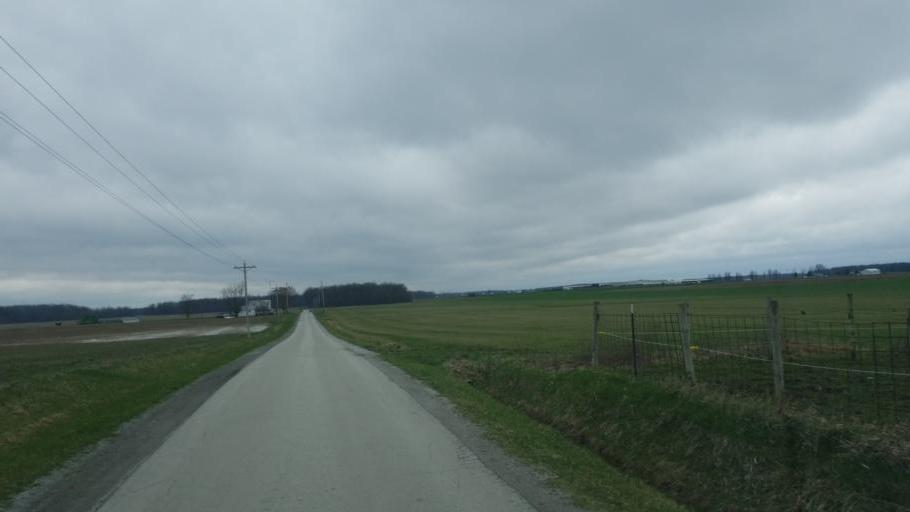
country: US
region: Ohio
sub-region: Hardin County
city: Forest
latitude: 40.7378
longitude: -83.4506
